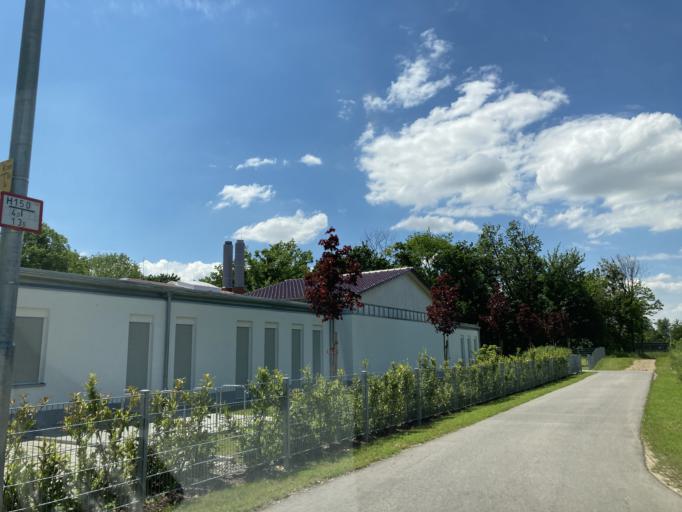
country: DE
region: Baden-Wuerttemberg
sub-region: Freiburg Region
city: Eschbach
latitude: 47.8981
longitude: 7.6325
